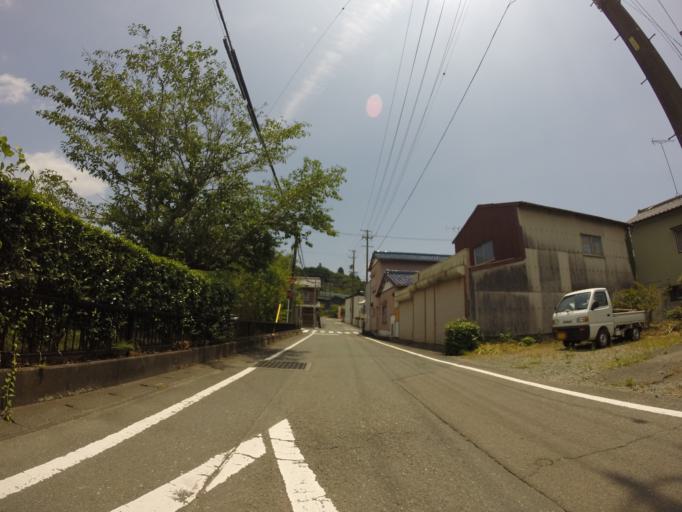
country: JP
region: Shizuoka
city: Kanaya
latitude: 34.8044
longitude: 138.0747
